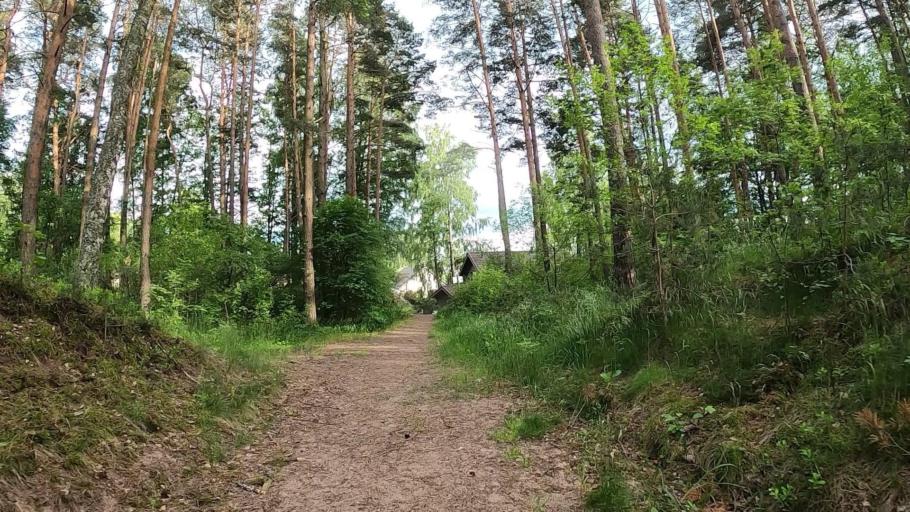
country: LV
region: Riga
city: Jaunciems
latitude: 57.0816
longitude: 24.1419
